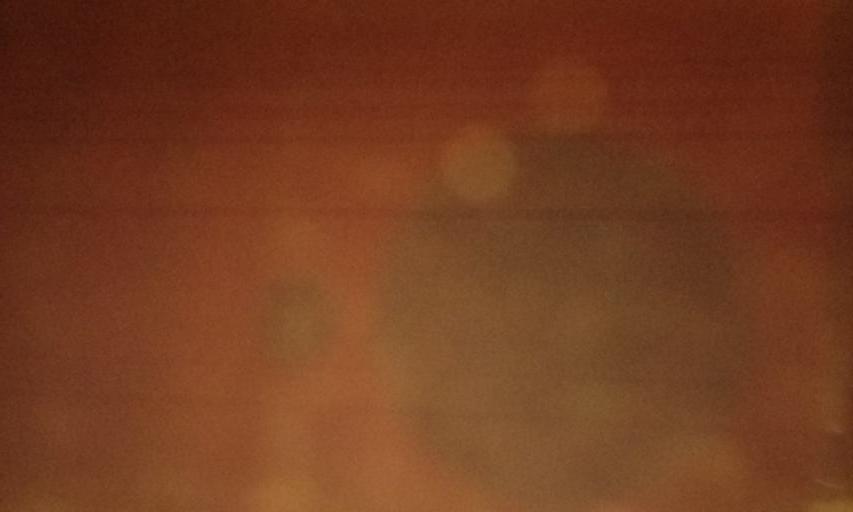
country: JP
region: Osaka
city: Suita
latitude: 34.7499
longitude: 135.4964
